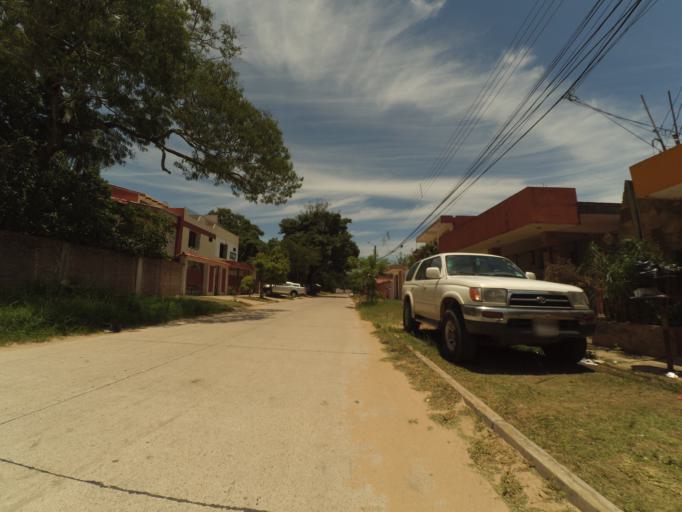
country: BO
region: Santa Cruz
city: Santa Cruz de la Sierra
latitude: -17.8094
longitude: -63.2241
